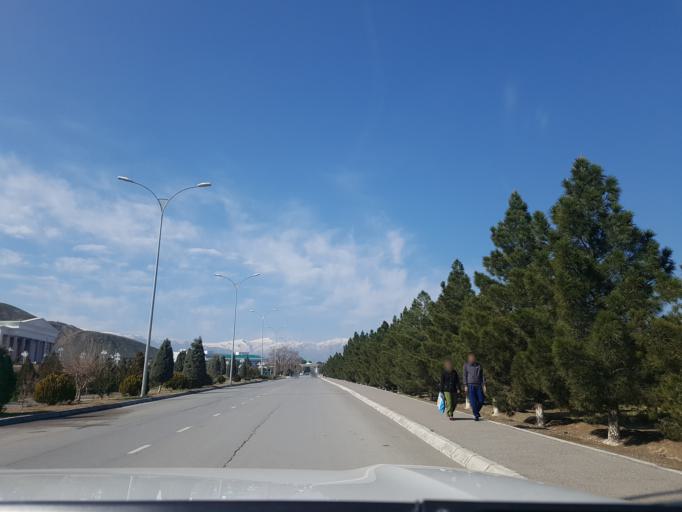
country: TM
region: Ahal
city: Baharly
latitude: 38.5179
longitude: 57.1828
